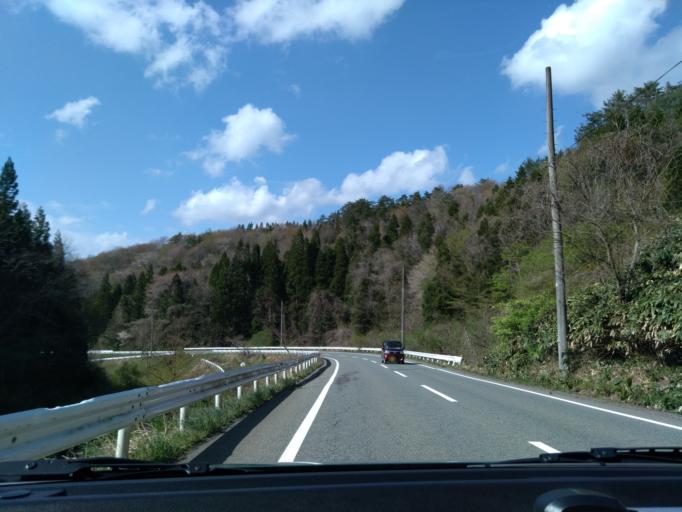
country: JP
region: Akita
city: Akita
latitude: 39.6973
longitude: 140.2211
